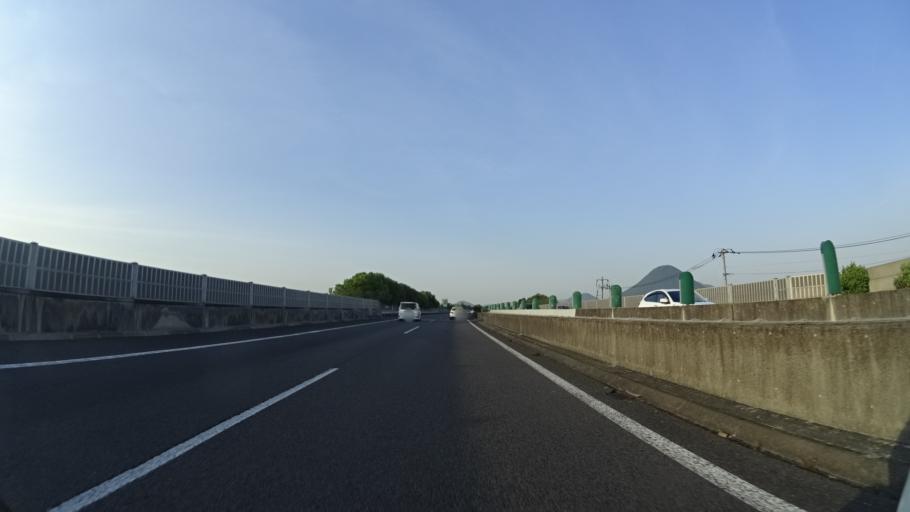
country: JP
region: Kagawa
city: Marugame
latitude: 34.2536
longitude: 133.8043
